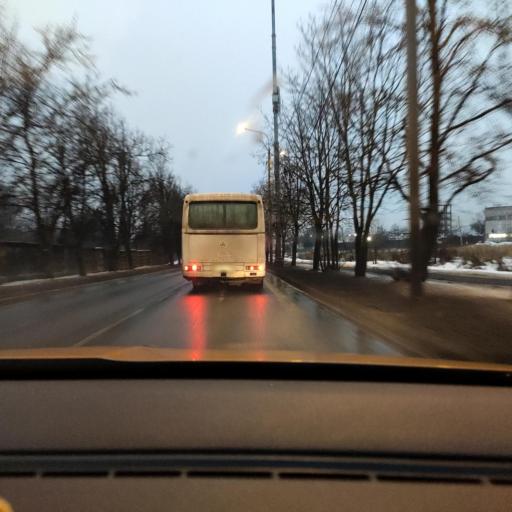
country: RU
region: Moskovskaya
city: Mosrentgen
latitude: 55.6171
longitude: 37.4614
